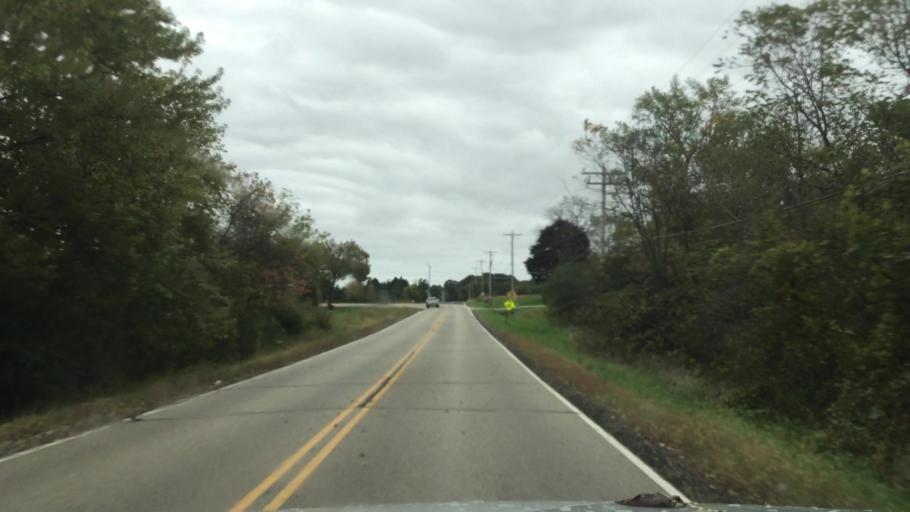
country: US
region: Wisconsin
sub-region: Racine County
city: Waterford
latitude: 42.7639
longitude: -88.1779
